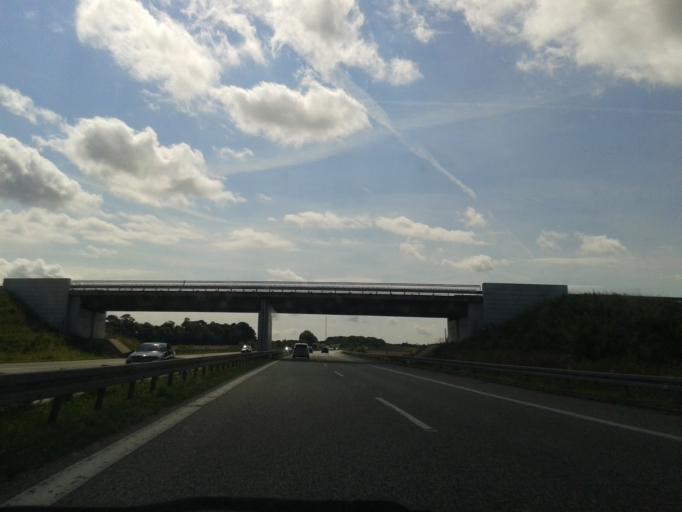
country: DE
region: Brandenburg
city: Schonfeld
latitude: 53.4412
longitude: 13.9912
